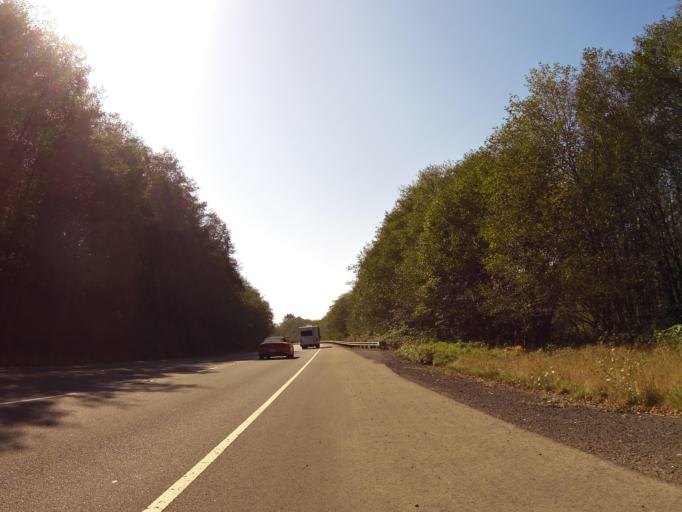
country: US
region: Oregon
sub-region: Tillamook County
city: Pacific City
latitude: 45.1468
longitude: -123.9647
